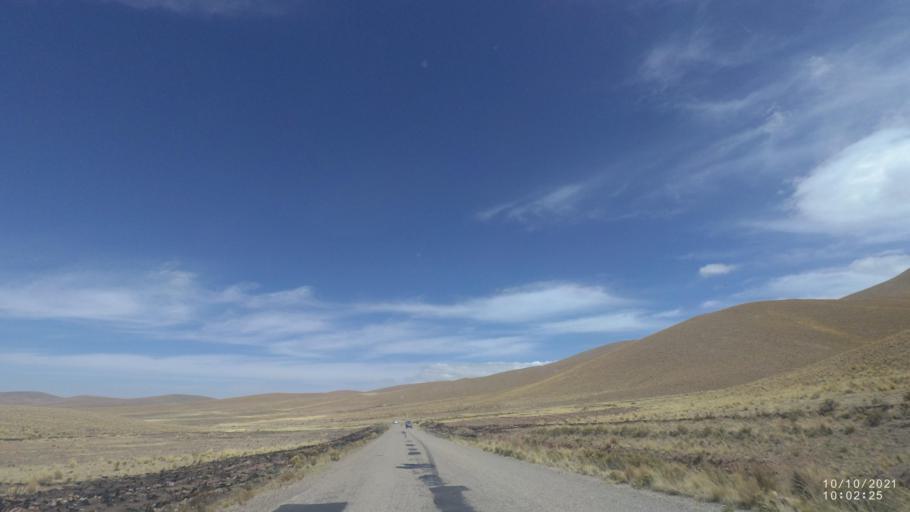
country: BO
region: La Paz
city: Eucaliptus
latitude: -17.3604
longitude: -67.4328
